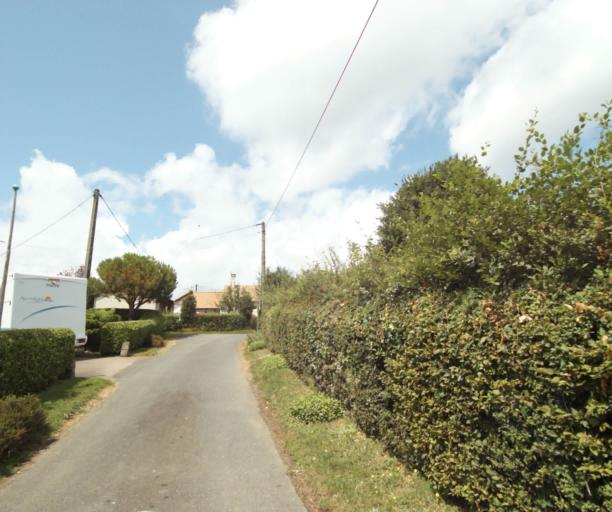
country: FR
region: Limousin
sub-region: Departement de la Correze
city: Sainte-Fortunade
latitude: 45.1989
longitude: 1.8455
